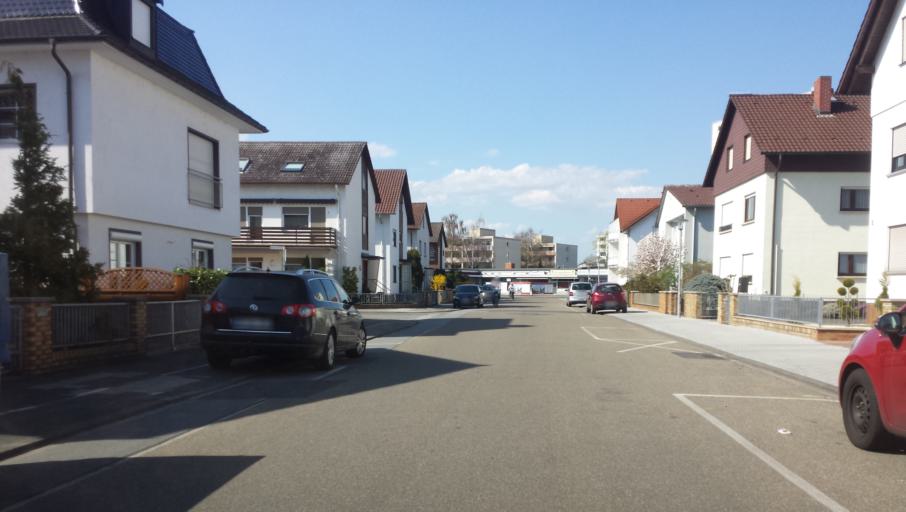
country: DE
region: Hesse
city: Lampertheim
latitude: 49.6025
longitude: 8.4801
